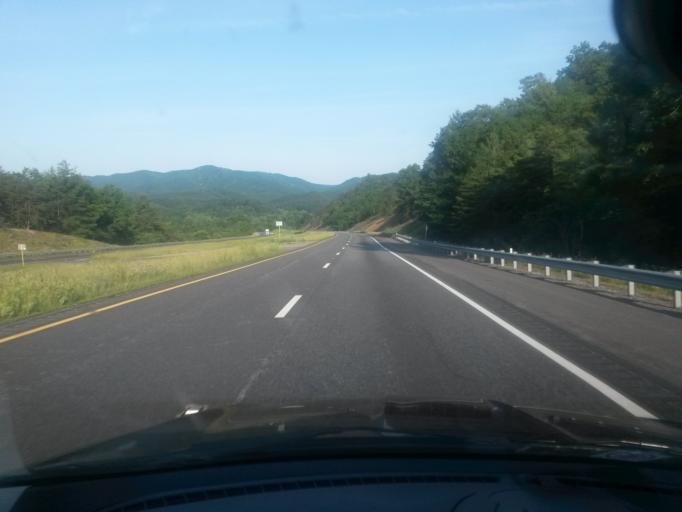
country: US
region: Virginia
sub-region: City of Covington
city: Covington
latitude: 37.8173
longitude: -80.0959
